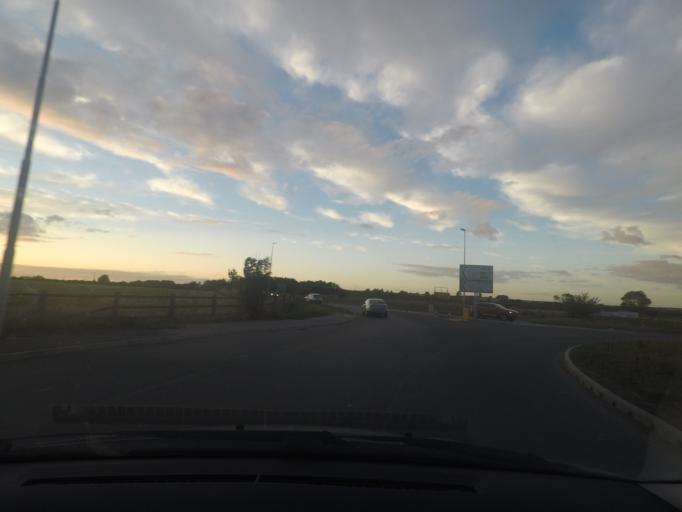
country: GB
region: England
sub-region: North Lincolnshire
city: Barnetby le Wold
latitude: 53.5824
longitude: -0.4116
